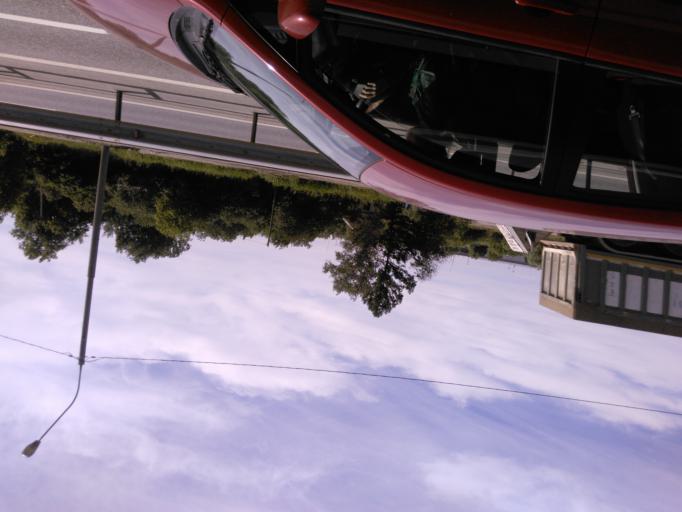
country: RU
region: Moskovskaya
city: Novopodrezkovo
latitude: 55.9516
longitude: 37.3486
